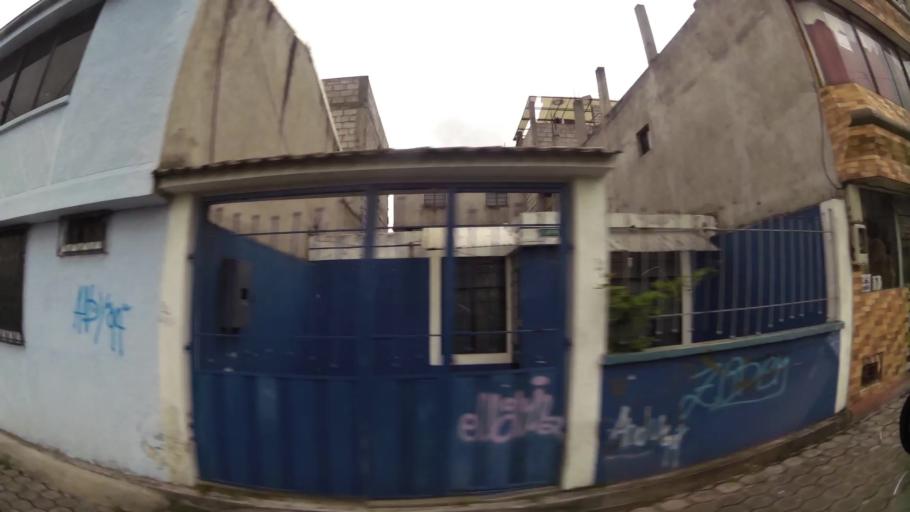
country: EC
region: Pichincha
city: Quito
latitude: -0.3143
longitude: -78.5468
